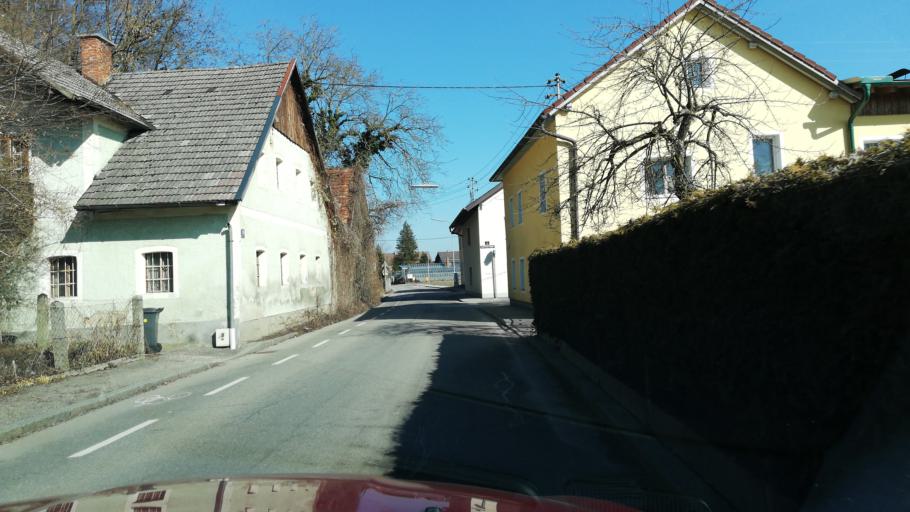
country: AT
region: Upper Austria
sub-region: Politischer Bezirk Vocklabruck
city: Redlham
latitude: 48.0150
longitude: 13.7302
